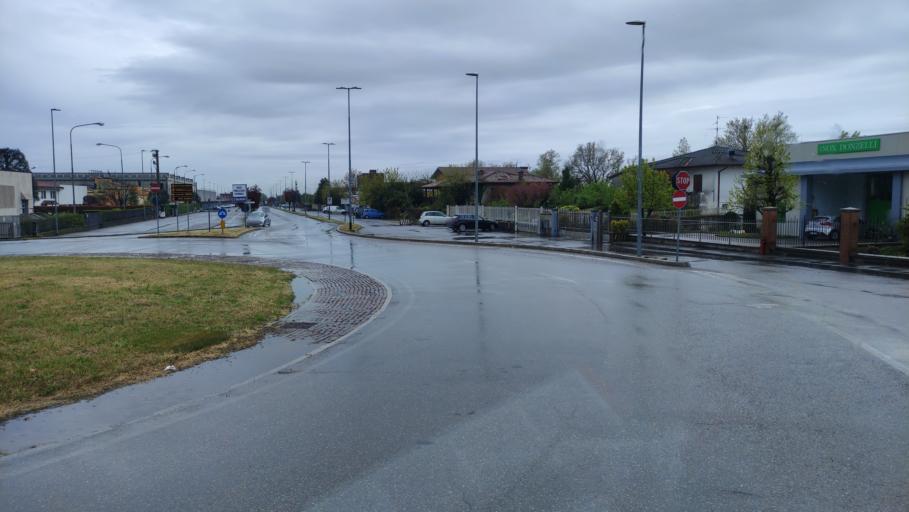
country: IT
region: Lombardy
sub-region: Provincia di Brescia
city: Rudiano
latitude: 45.5001
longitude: 9.8796
